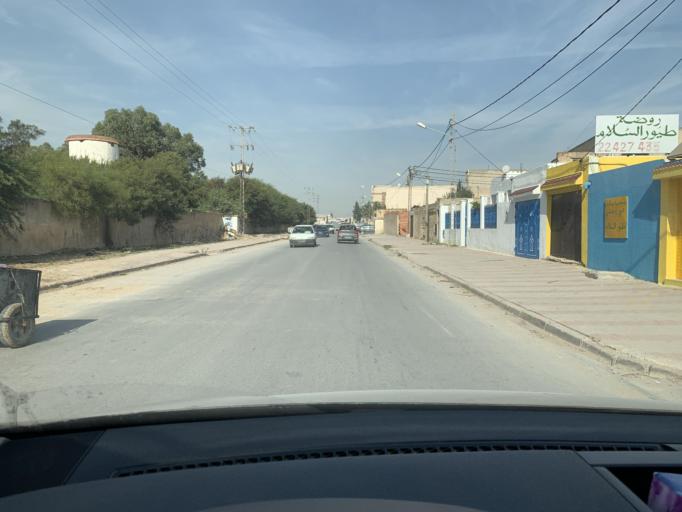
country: TN
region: Manouba
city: Manouba
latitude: 36.8177
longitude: 10.1176
